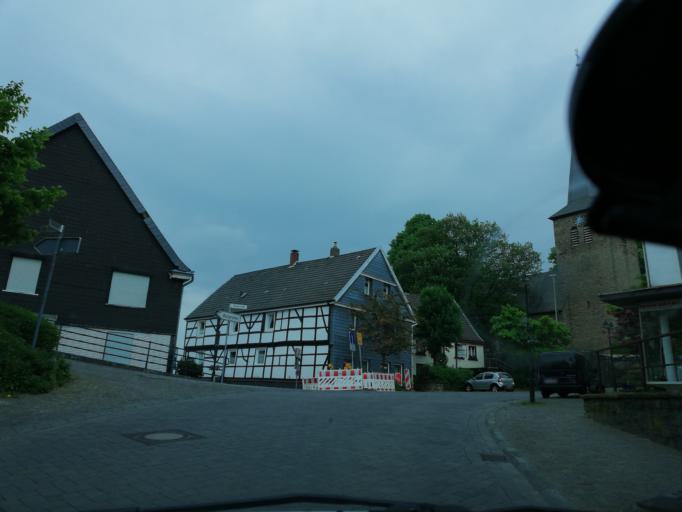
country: DE
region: North Rhine-Westphalia
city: Wetter (Ruhr)
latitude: 51.3729
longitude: 7.3831
